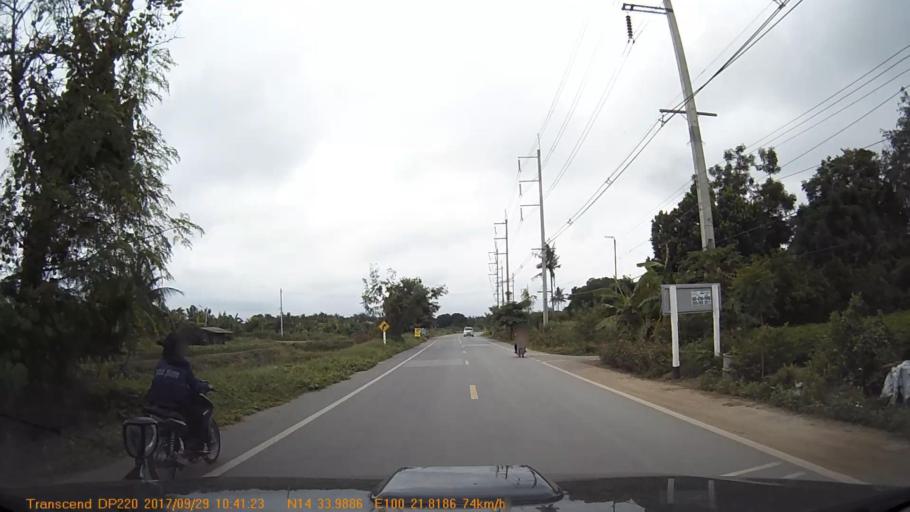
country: TH
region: Ang Thong
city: Wiset Chaichan
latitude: 14.5664
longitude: 100.3637
